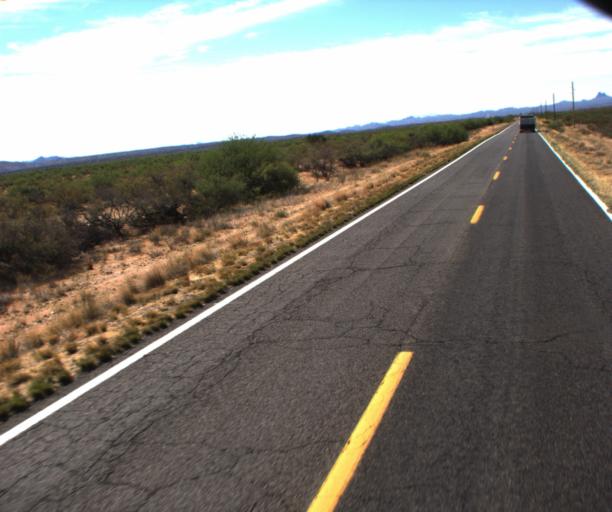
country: US
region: Arizona
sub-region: Yavapai County
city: Congress
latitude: 34.0951
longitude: -112.8287
